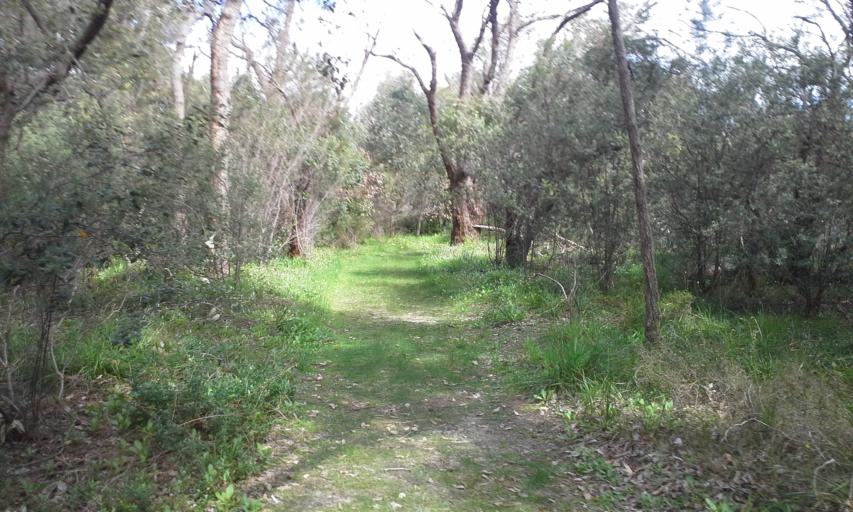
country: AU
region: Western Australia
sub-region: City of Perth
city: West Perth
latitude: -31.9613
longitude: 115.8384
